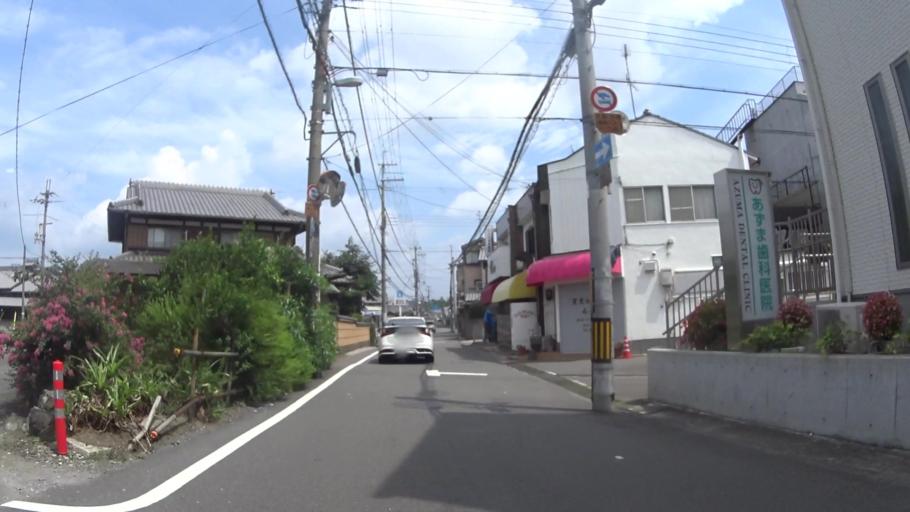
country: JP
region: Kyoto
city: Muko
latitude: 34.9429
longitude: 135.7330
